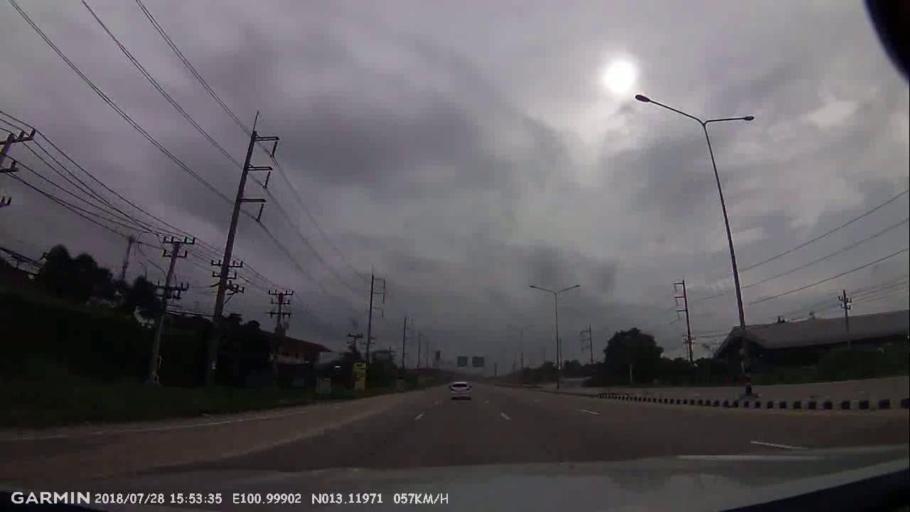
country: TH
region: Chon Buri
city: Ban Talat Bueng
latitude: 13.1197
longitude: 100.9988
